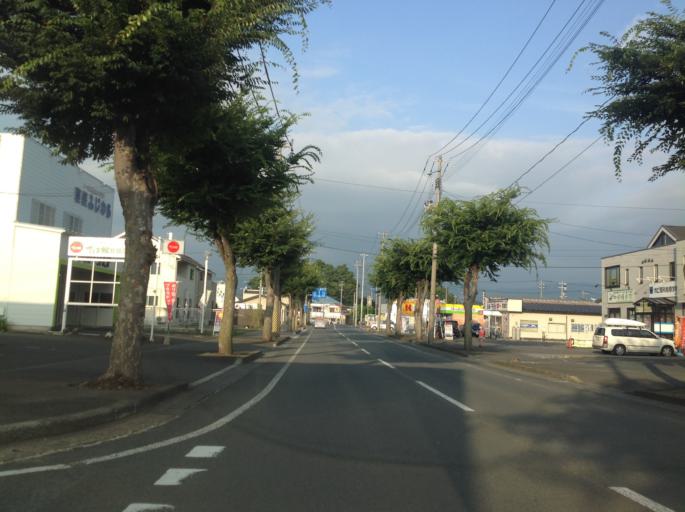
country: JP
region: Iwate
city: Morioka-shi
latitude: 39.5523
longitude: 141.1651
